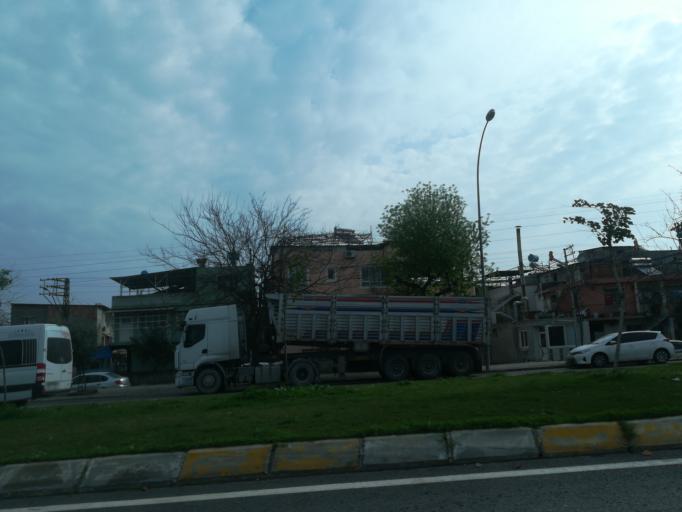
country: TR
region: Adana
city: Yuregir
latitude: 36.9949
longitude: 35.3598
